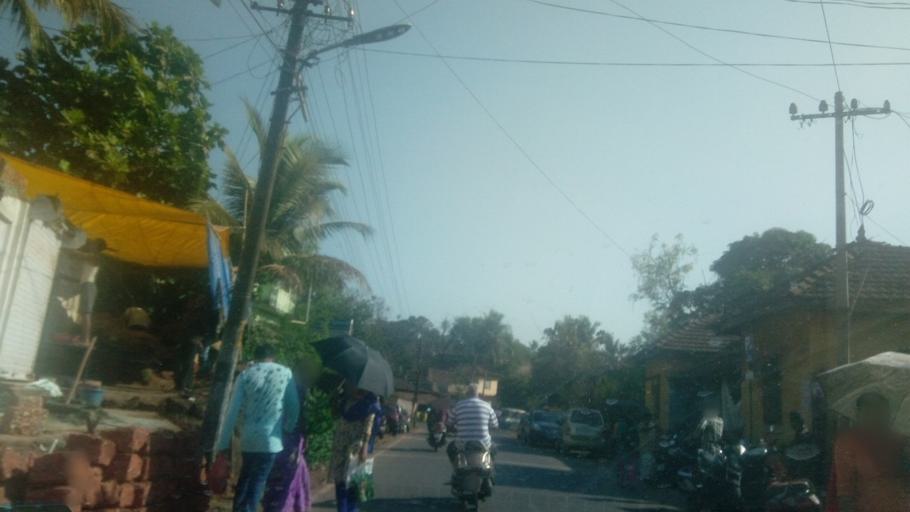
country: IN
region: Goa
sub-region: North Goa
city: Jua
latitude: 15.5145
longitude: 73.9610
